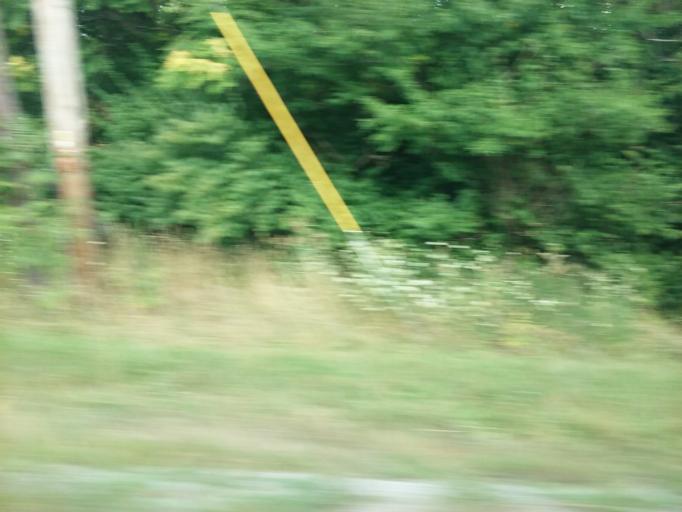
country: US
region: Ohio
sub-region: Wood County
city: Bowling Green
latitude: 41.3222
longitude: -83.6503
